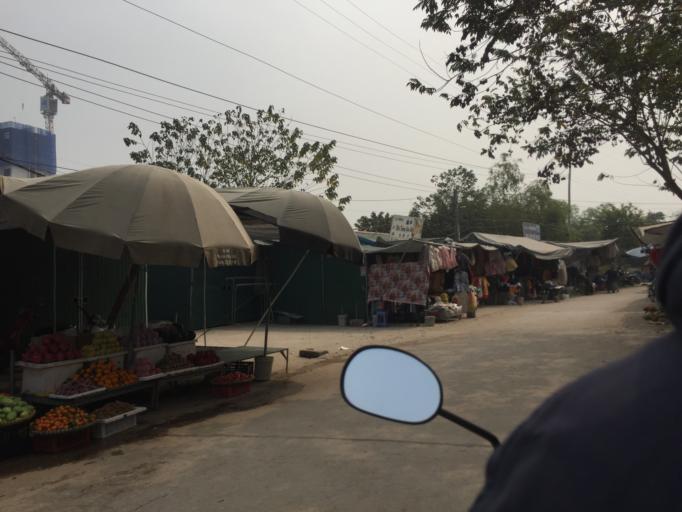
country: VN
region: Hung Yen
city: Van Giang
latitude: 20.9637
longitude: 105.9183
